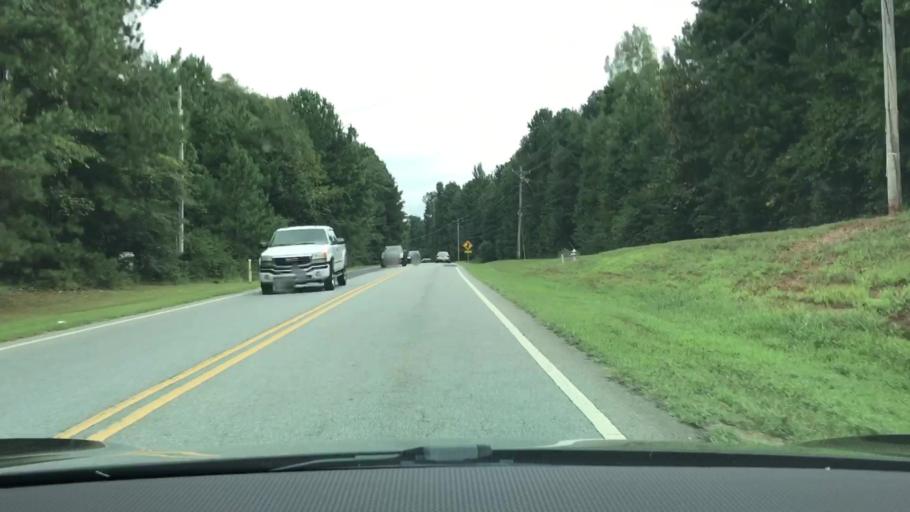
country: US
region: Georgia
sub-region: Barrow County
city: Auburn
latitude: 34.0927
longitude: -83.8685
